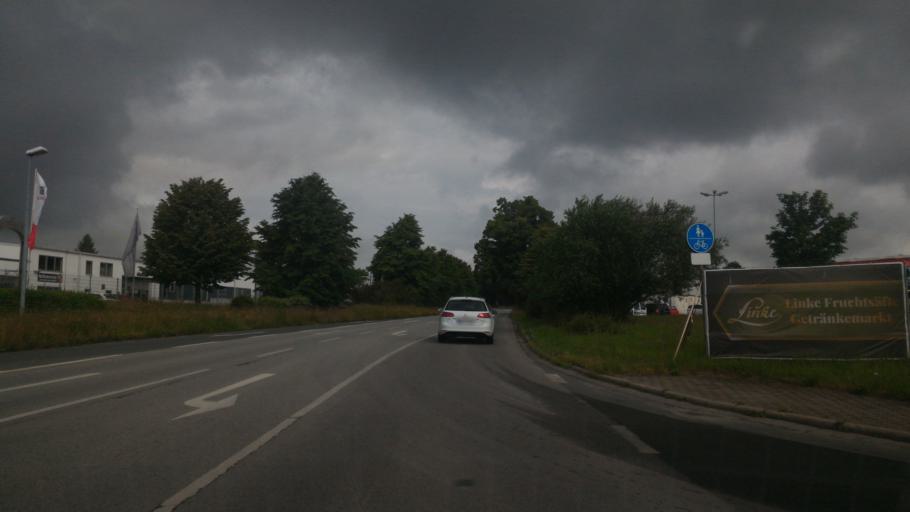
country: DE
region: Saxony
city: Neugersdorf
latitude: 50.9797
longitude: 14.6280
